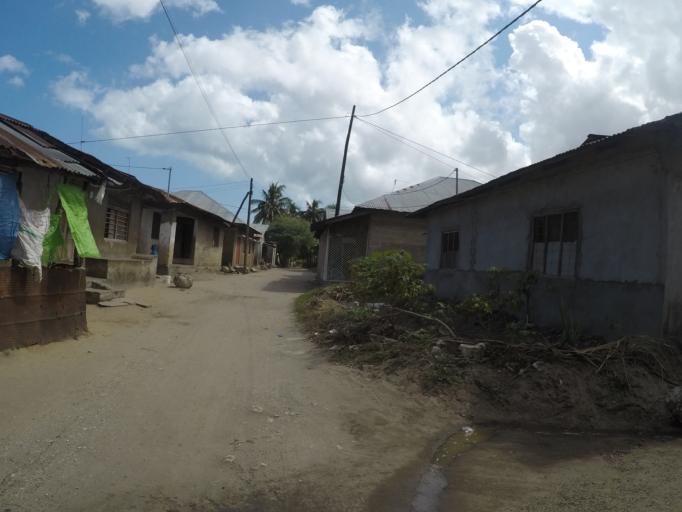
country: TZ
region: Zanzibar Urban/West
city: Zanzibar
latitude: -6.1792
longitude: 39.2120
